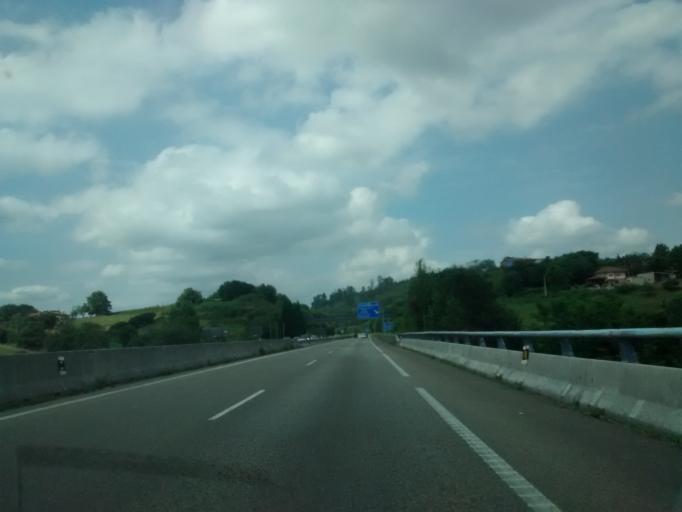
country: ES
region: Asturias
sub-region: Province of Asturias
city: Pola de Siero
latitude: 43.3643
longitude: -5.6828
